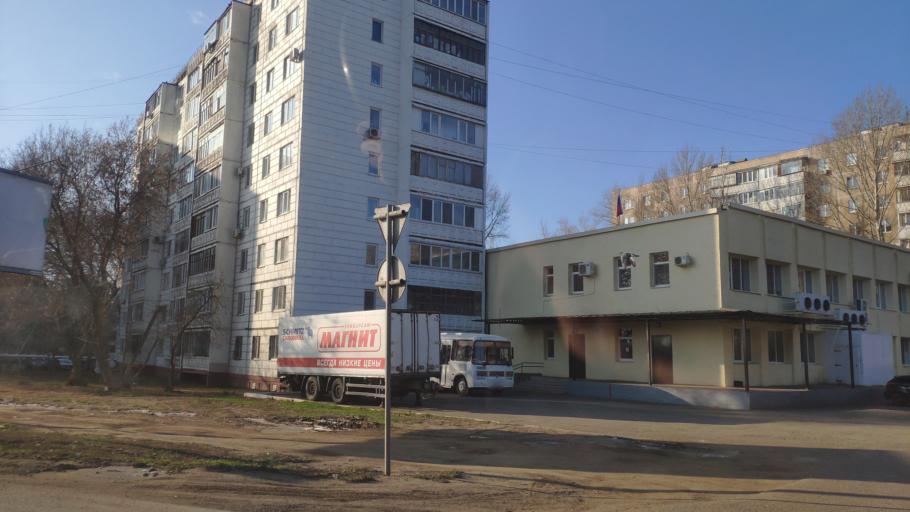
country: RU
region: Orenburg
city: Prigorodnyy
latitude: 51.7773
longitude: 55.1912
